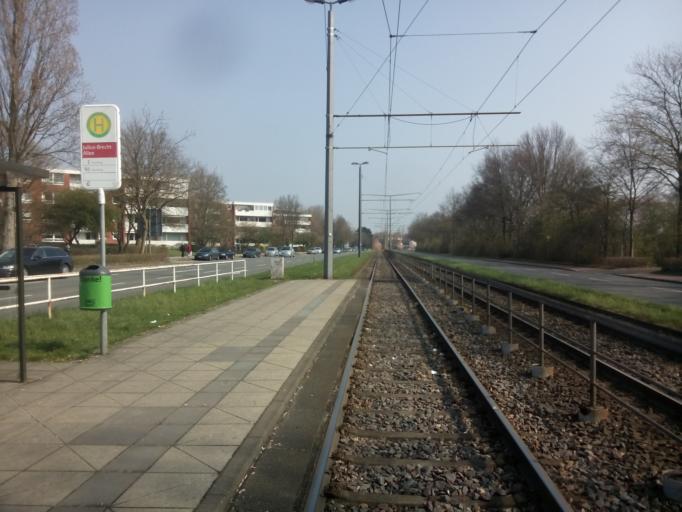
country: DE
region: Bremen
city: Bremen
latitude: 53.0750
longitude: 8.8698
